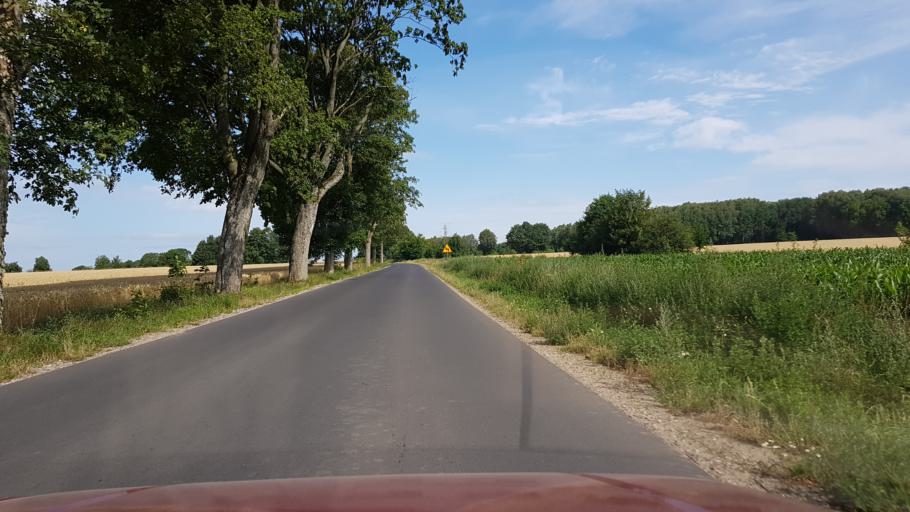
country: PL
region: West Pomeranian Voivodeship
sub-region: Powiat koszalinski
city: Polanow
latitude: 54.1641
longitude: 16.6128
